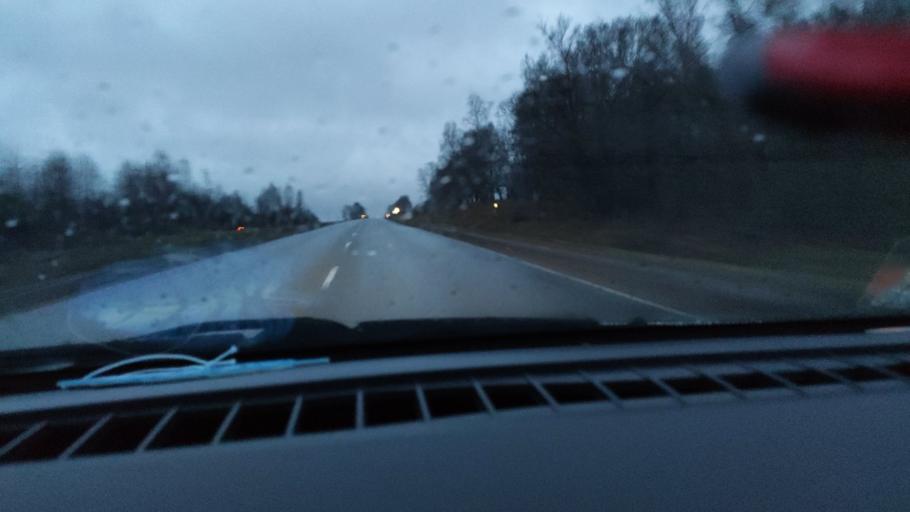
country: RU
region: Udmurtiya
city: Mozhga
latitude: 56.3184
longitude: 52.3249
